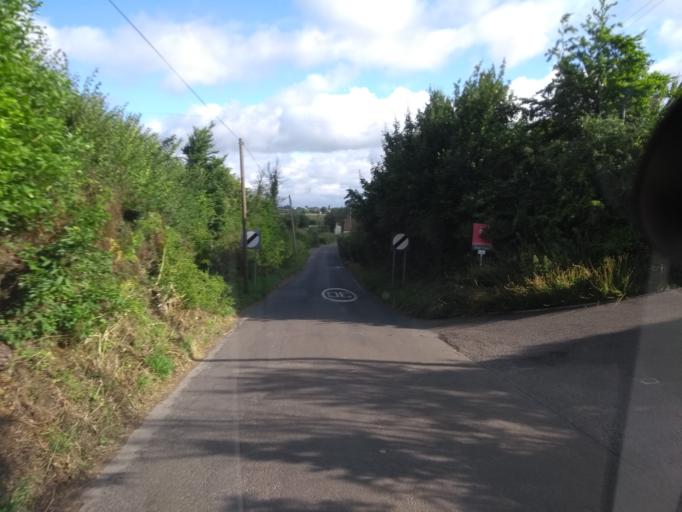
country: GB
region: England
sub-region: Somerset
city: Creech Saint Michael
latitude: 51.0258
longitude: -2.9733
